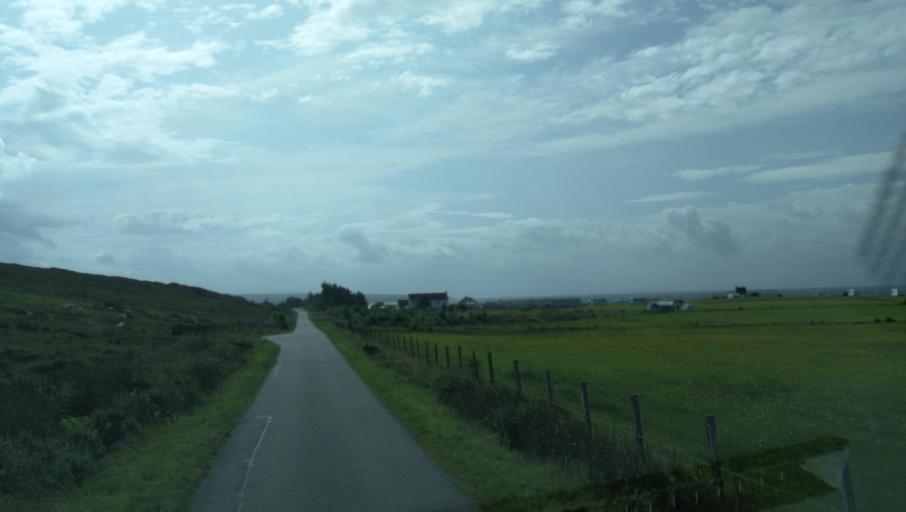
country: GB
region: Scotland
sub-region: Highland
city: Portree
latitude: 57.7437
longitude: -5.7635
